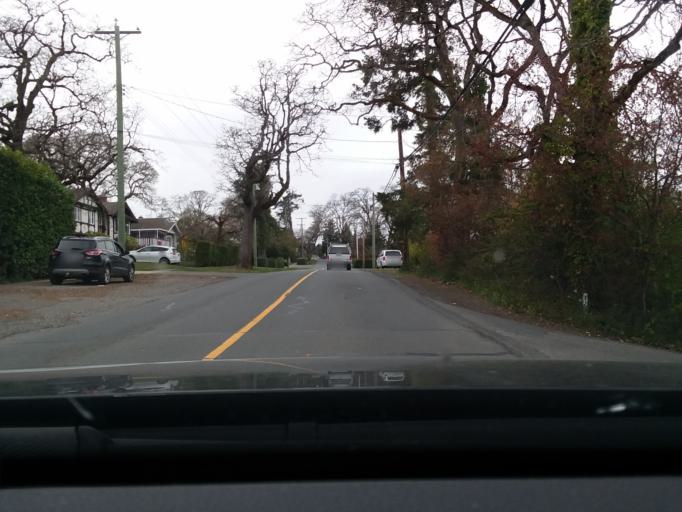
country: CA
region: British Columbia
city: Victoria
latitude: 48.4786
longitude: -123.4126
